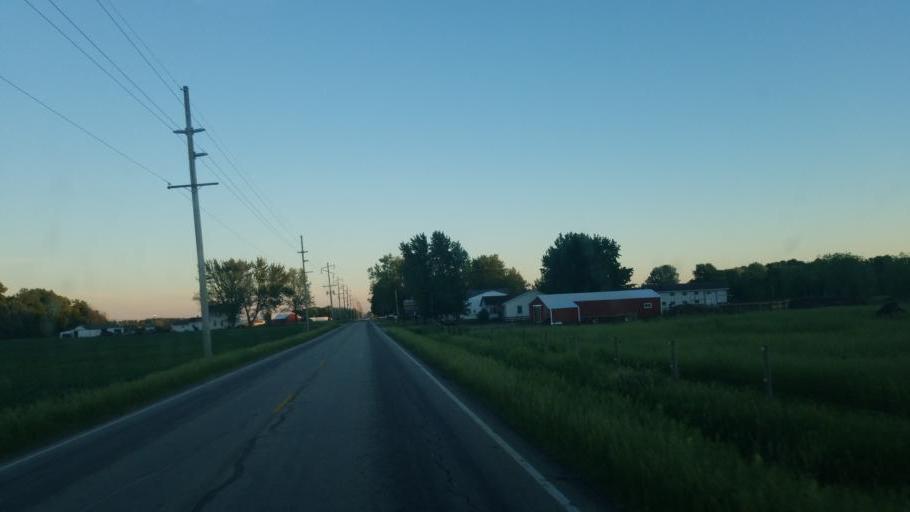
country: US
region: Indiana
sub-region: Elkhart County
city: Nappanee
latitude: 41.3860
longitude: -86.0009
